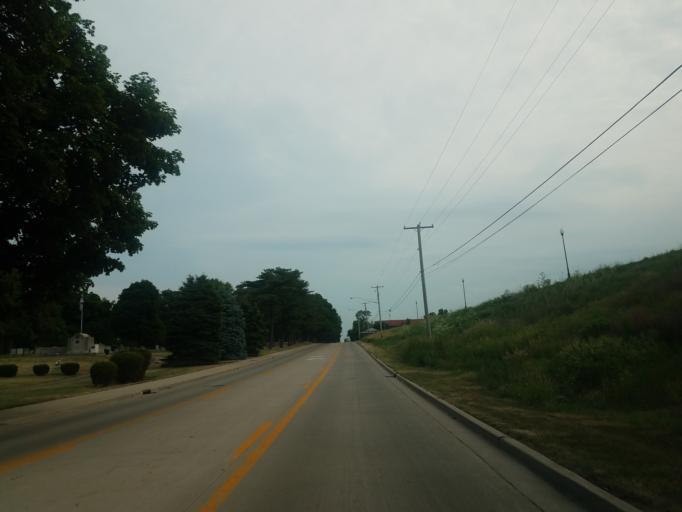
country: US
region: Illinois
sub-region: McLean County
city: Bloomington
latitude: 40.4664
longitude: -89.0063
